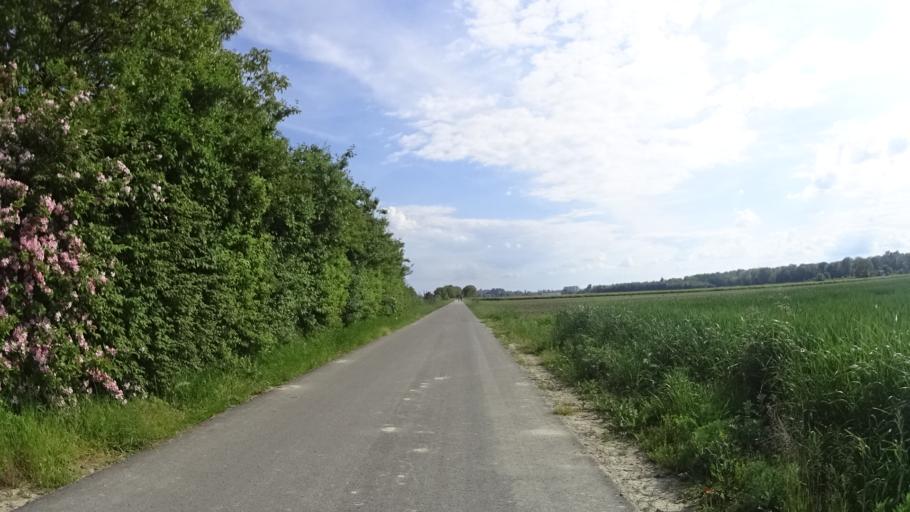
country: DE
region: Baden-Wuerttemberg
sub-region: Freiburg Region
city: Breisach am Rhein
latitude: 48.0606
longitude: 7.5886
